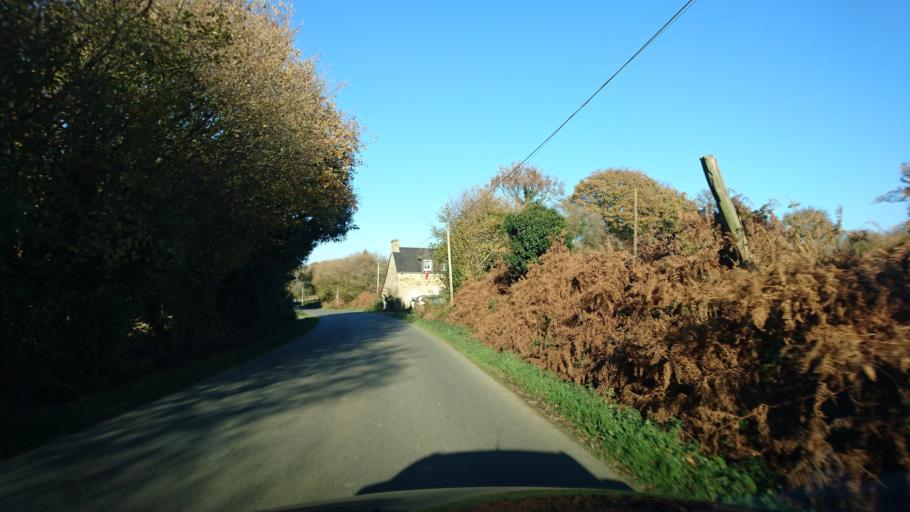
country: FR
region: Brittany
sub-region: Departement des Cotes-d'Armor
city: Pedernec
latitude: 48.5790
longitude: -3.2614
